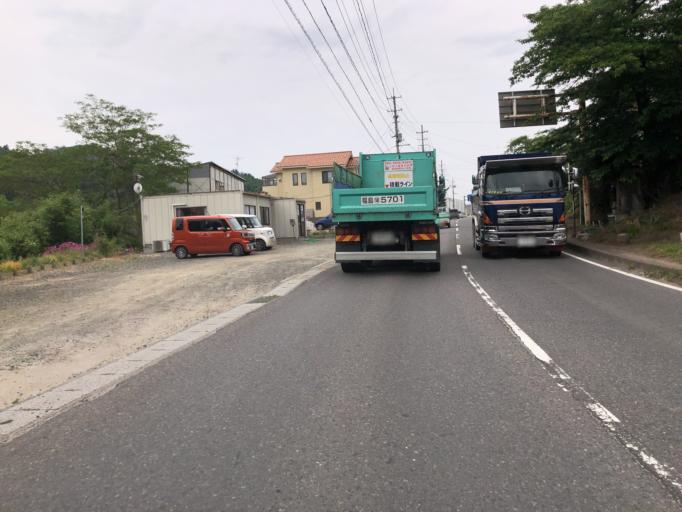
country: JP
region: Fukushima
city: Funehikimachi-funehiki
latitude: 37.4344
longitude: 140.5894
